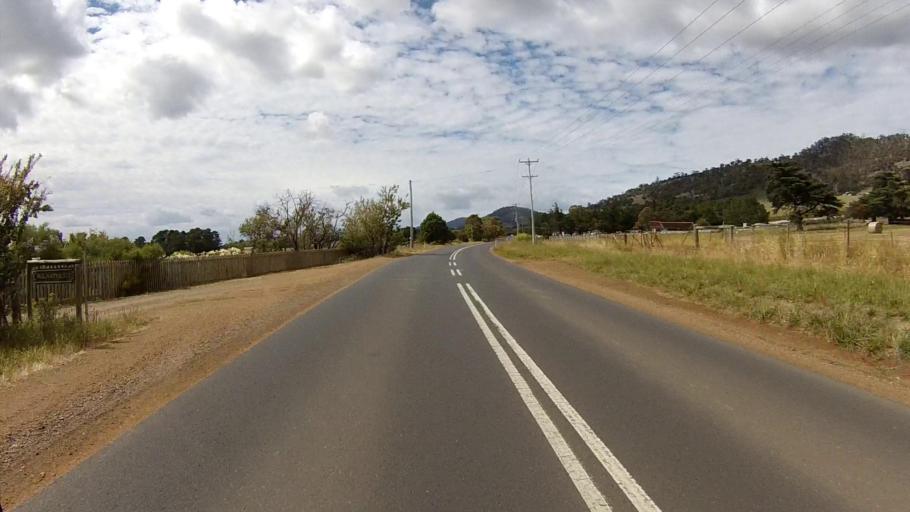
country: AU
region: Tasmania
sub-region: Clarence
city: Cambridge
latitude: -42.7905
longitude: 147.4178
